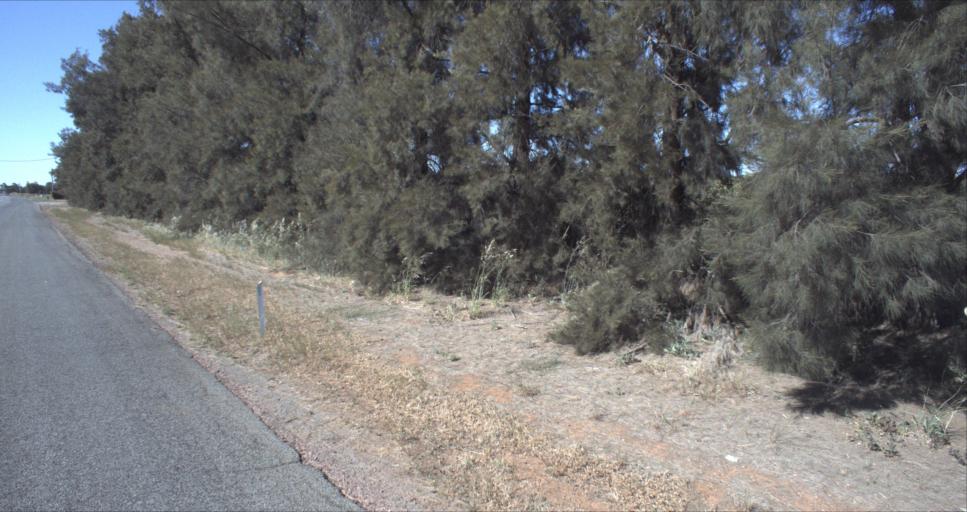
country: AU
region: New South Wales
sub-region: Leeton
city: Leeton
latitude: -34.5661
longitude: 146.3826
